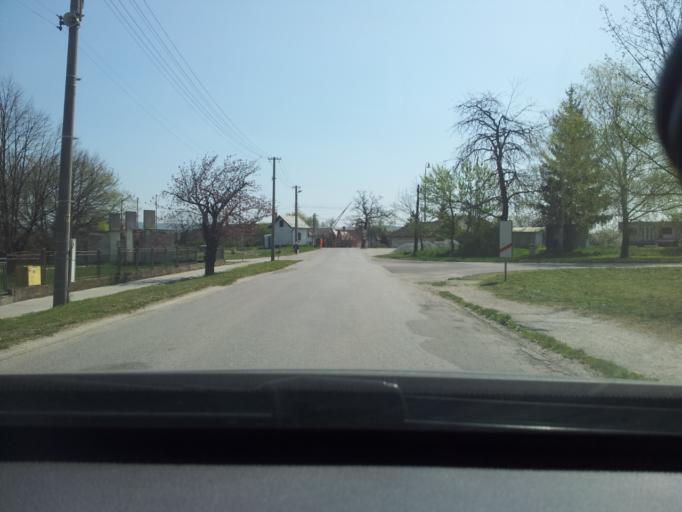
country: SK
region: Nitriansky
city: Partizanske
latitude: 48.6093
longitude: 18.2761
